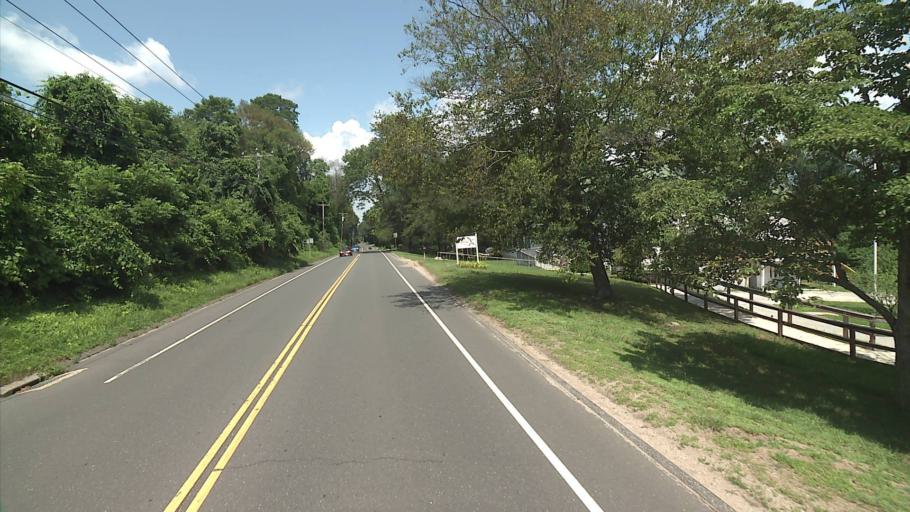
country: US
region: Connecticut
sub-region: Middlesex County
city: East Haddam
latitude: 41.4285
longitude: -72.4511
